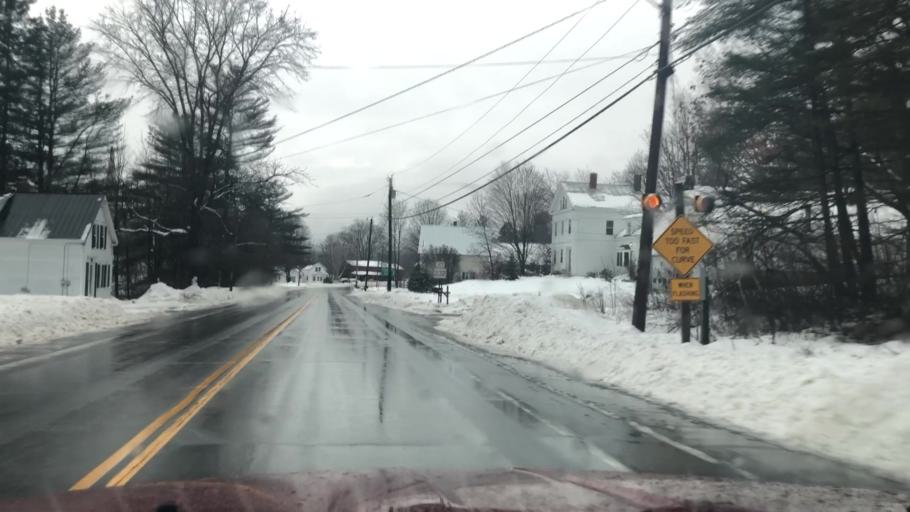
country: US
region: Maine
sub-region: Oxford County
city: Rumford
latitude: 44.5004
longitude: -70.6693
